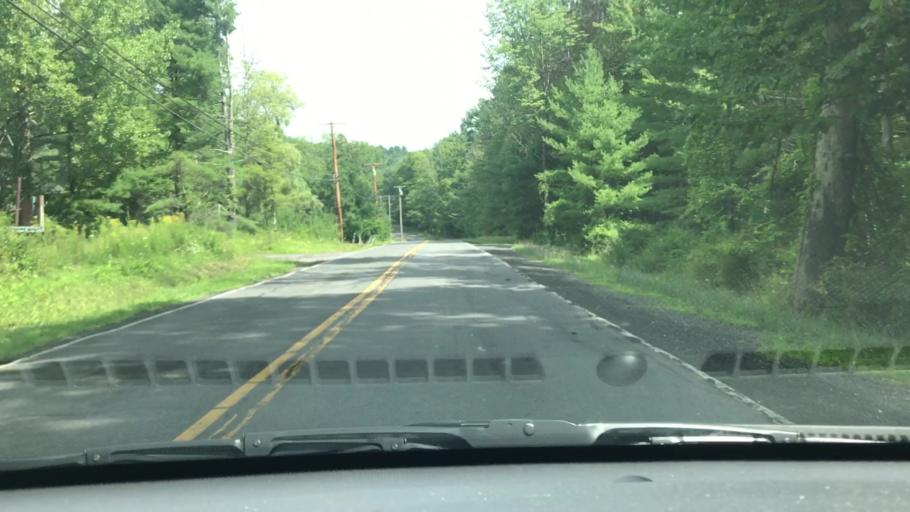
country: US
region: New York
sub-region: Ulster County
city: Shokan
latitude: 41.9739
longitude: -74.2774
